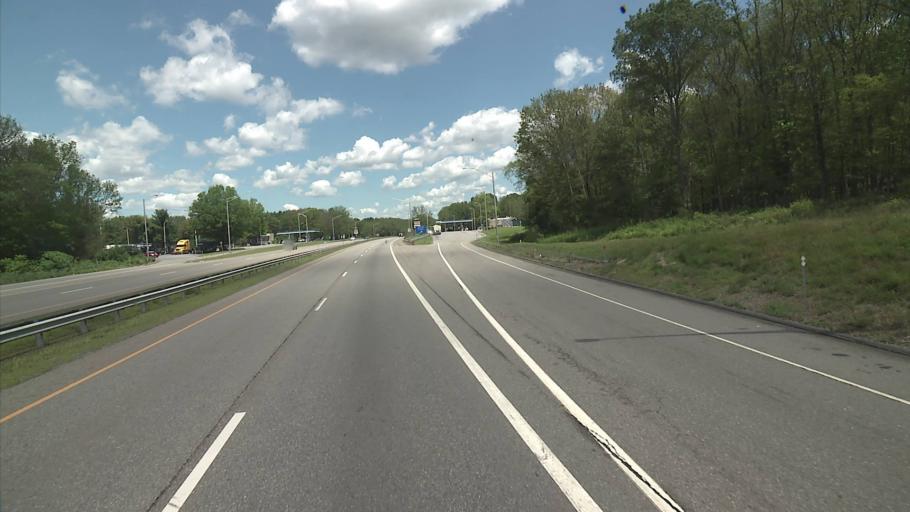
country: US
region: Connecticut
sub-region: Windham County
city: Wauregan
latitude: 41.7523
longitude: -71.8785
